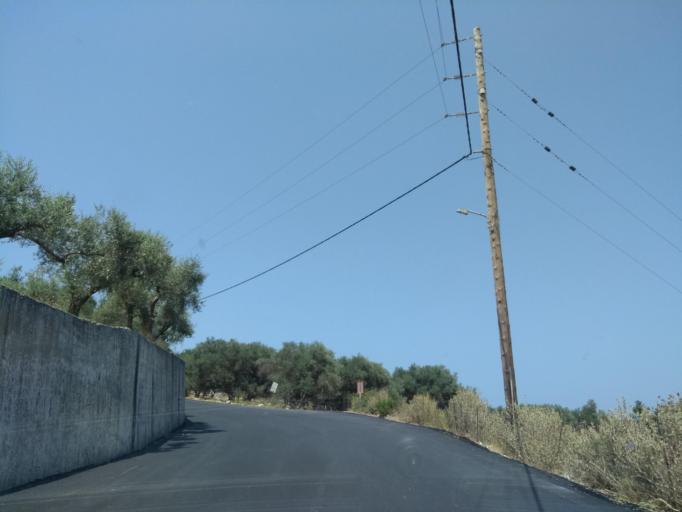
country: GR
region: Crete
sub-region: Nomos Chanias
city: Georgioupolis
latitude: 35.3202
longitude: 24.3003
